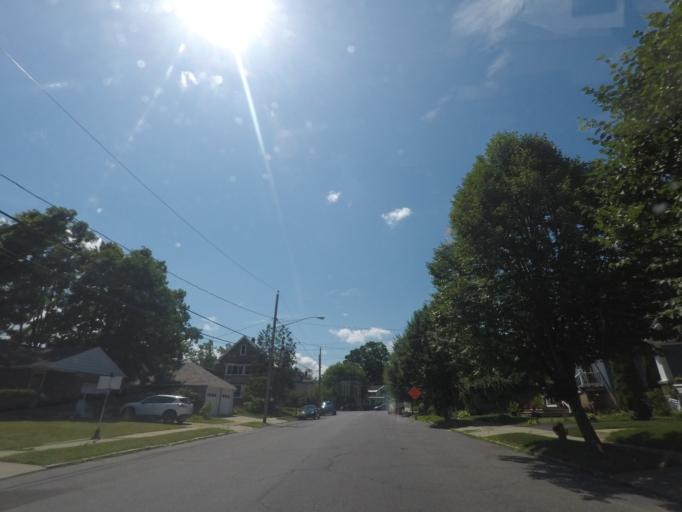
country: US
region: New York
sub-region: Schenectady County
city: Rotterdam
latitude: 42.7955
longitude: -73.9610
